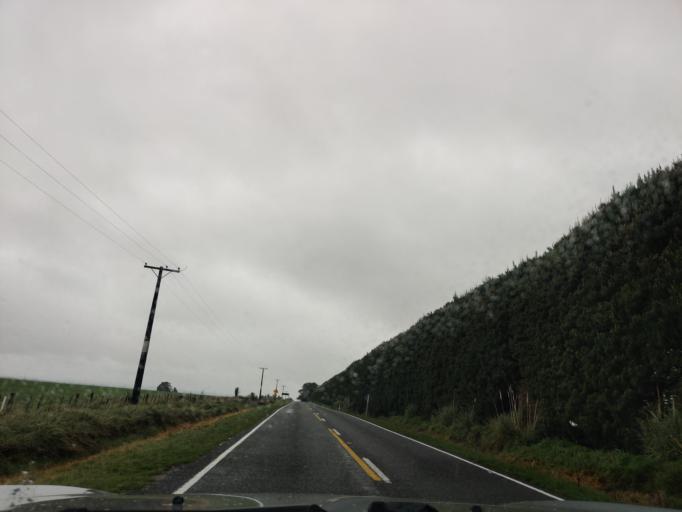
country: NZ
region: Manawatu-Wanganui
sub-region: Palmerston North City
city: Palmerston North
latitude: -40.0431
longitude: 176.2513
